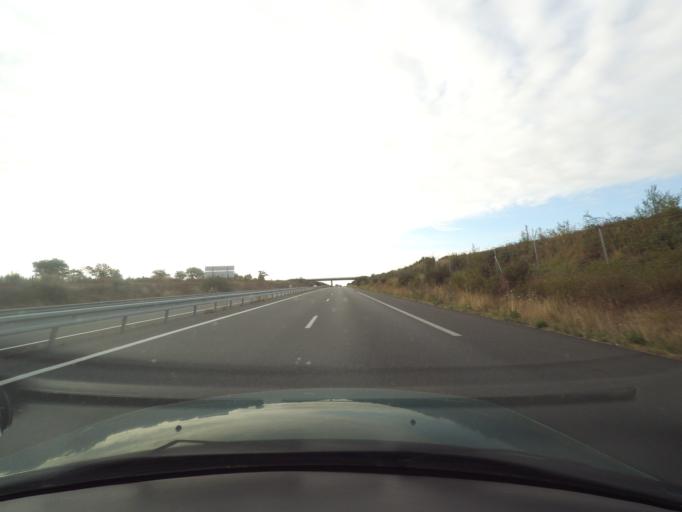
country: FR
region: Poitou-Charentes
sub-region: Departement des Deux-Sevres
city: Saint-Pierre-des-Echaubrognes
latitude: 46.9494
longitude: -0.7674
